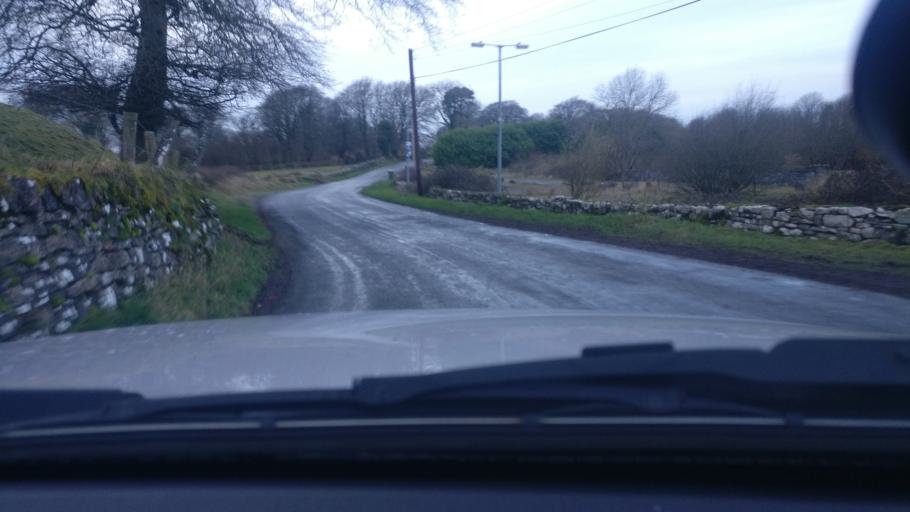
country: IE
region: Connaught
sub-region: County Galway
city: Loughrea
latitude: 53.1642
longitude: -8.5758
